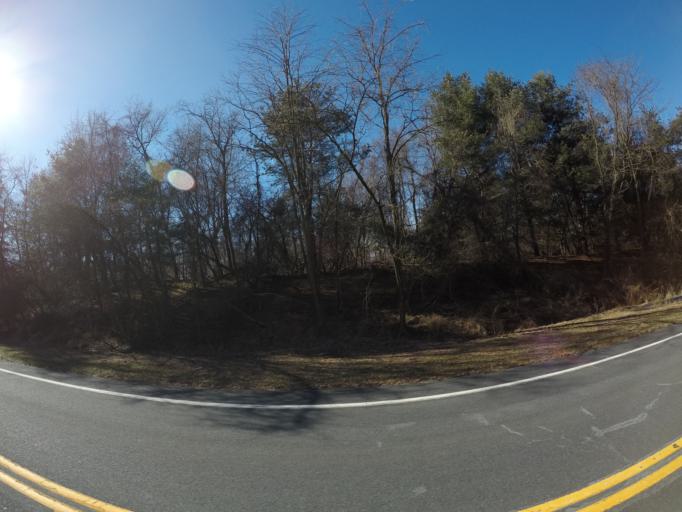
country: US
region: Maryland
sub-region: Howard County
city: Columbia
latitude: 39.2454
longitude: -76.8276
